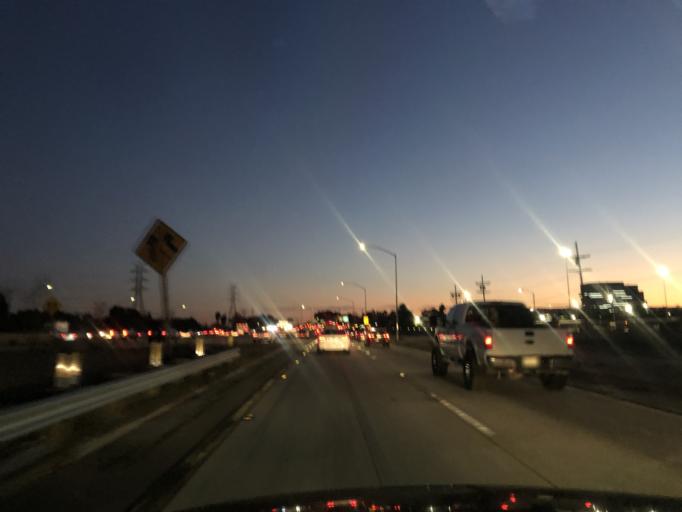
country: US
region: California
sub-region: Los Angeles County
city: West Rancho Dominguez
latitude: 33.8665
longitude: -118.2854
